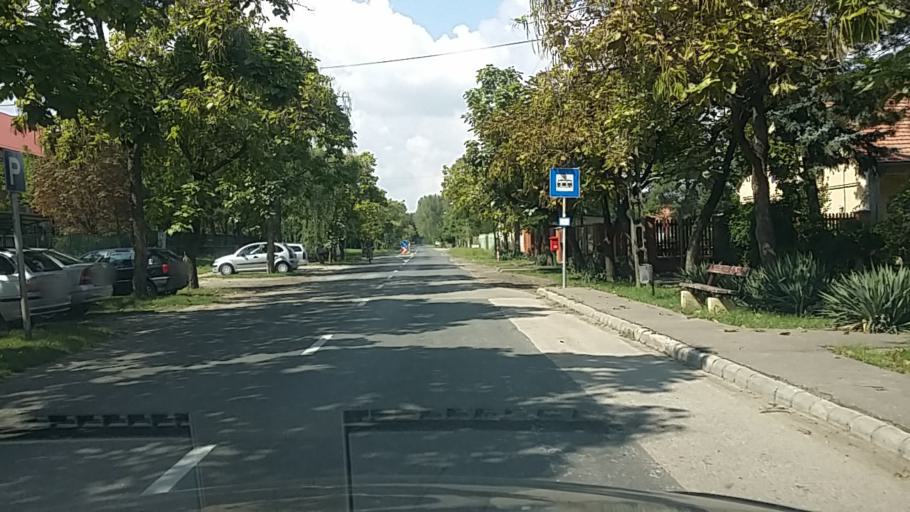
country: HU
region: Bacs-Kiskun
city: Tiszaalpar
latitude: 46.7531
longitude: 20.0343
